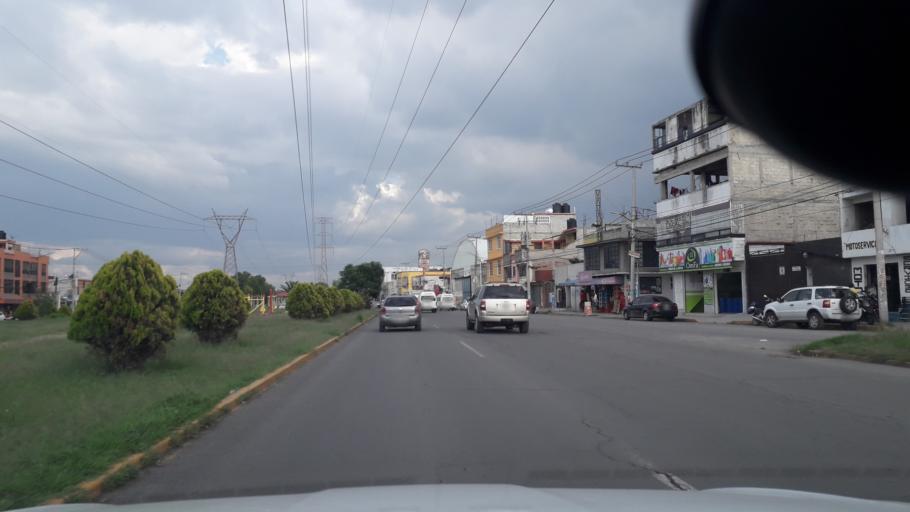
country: MX
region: Mexico
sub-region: Tultitlan
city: Fuentes del Valle
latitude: 19.6406
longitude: -99.1336
